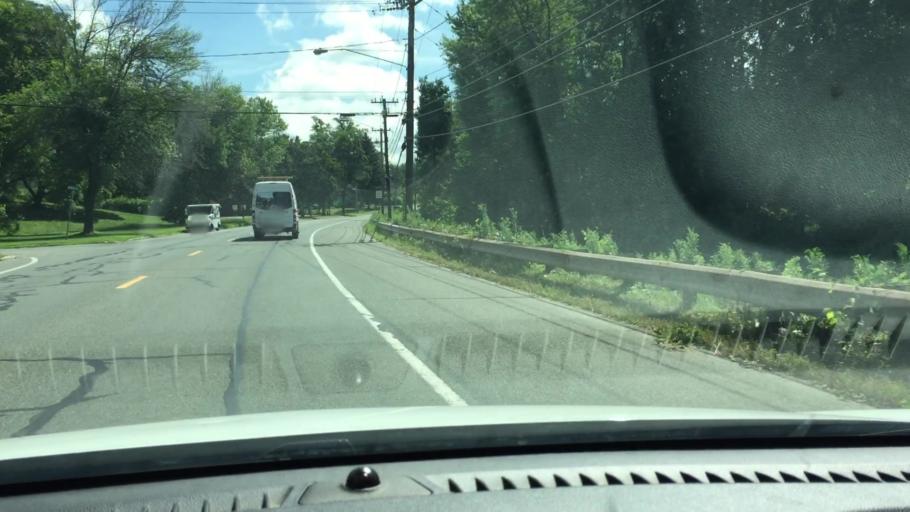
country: US
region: Massachusetts
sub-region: Berkshire County
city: Pittsfield
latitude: 42.4404
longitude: -73.2907
